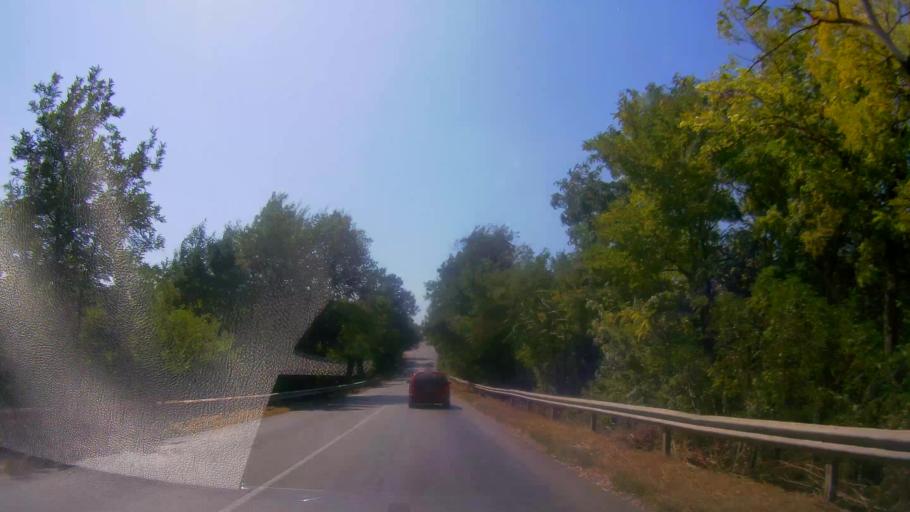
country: BG
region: Veliko Turnovo
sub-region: Obshtina Gorna Oryakhovitsa
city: Purvomaytsi
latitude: 43.2425
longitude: 25.6429
